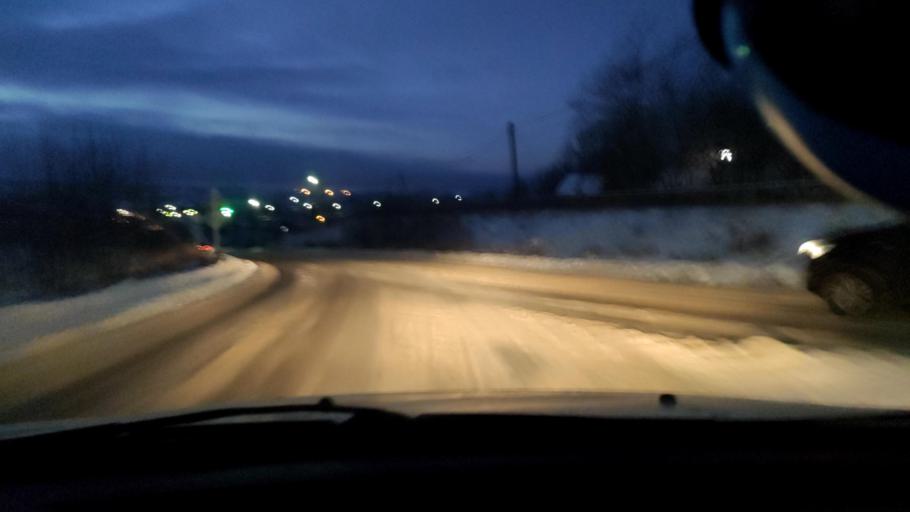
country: RU
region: Perm
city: Kultayevo
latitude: 57.9265
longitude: 55.8841
